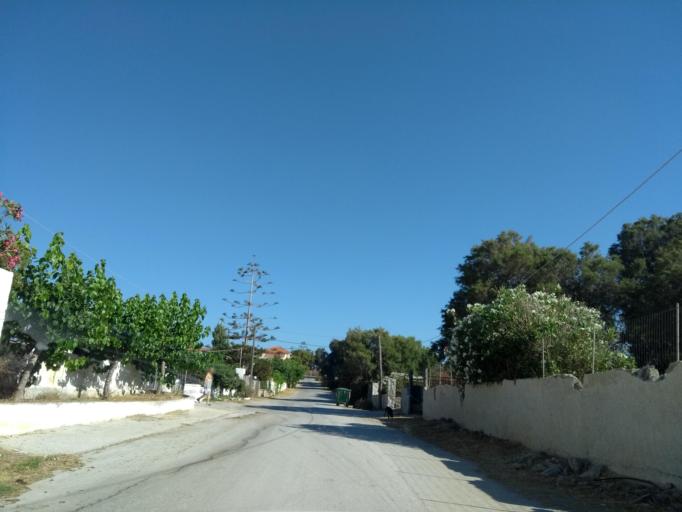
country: GR
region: Crete
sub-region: Nomos Chanias
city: Pithari
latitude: 35.5911
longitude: 24.0907
